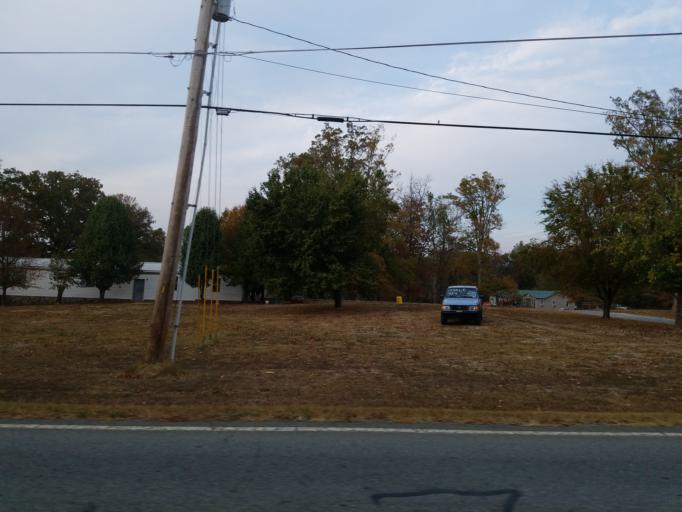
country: US
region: Georgia
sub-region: Gordon County
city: Calhoun
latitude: 34.6012
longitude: -84.9175
